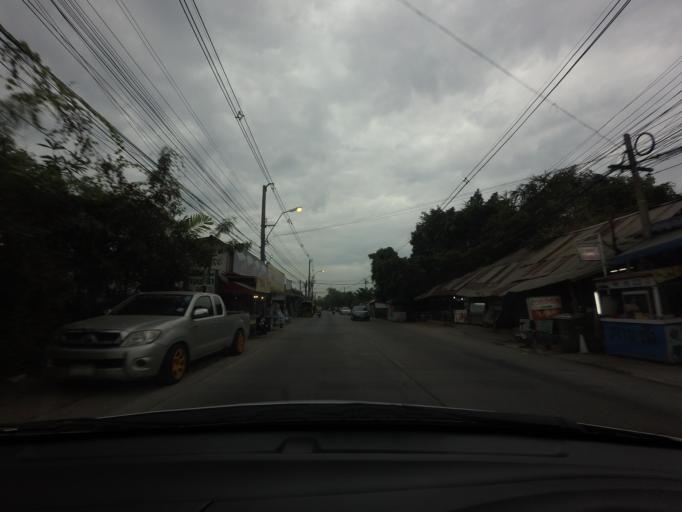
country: TH
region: Bangkok
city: Yan Nawa
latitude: 13.6784
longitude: 100.5608
